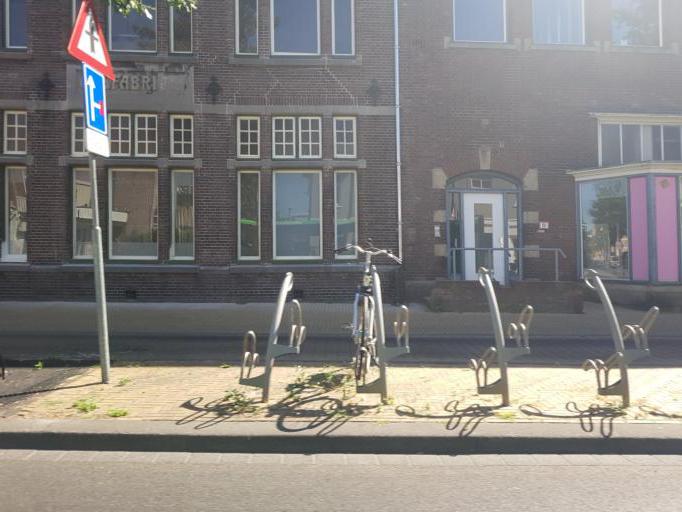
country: NL
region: Gelderland
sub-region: Gemeente Apeldoorn
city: Apeldoorn
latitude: 52.2141
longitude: 5.9665
